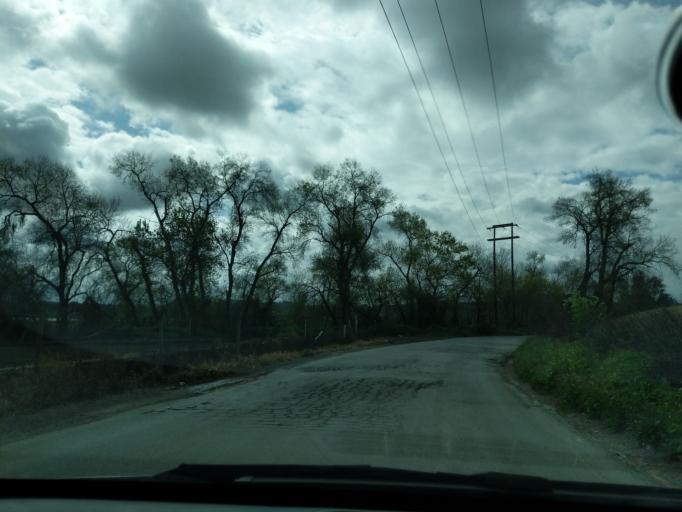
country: US
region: California
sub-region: San Benito County
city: Aromas
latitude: 36.9078
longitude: -121.6757
